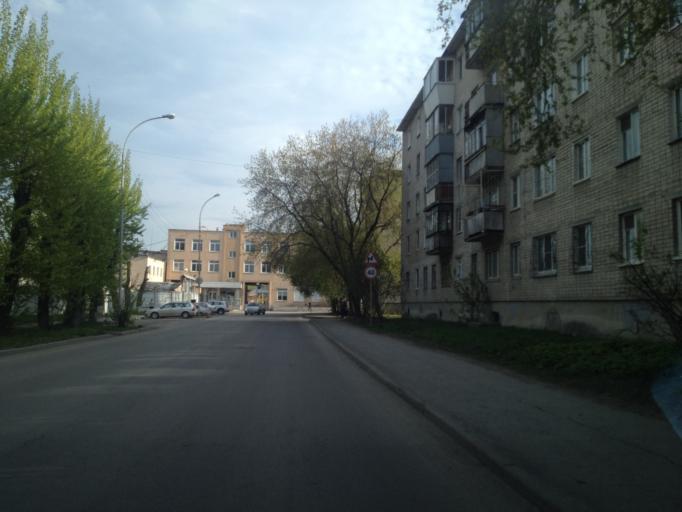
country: RU
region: Sverdlovsk
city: Yekaterinburg
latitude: 56.8409
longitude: 60.6640
